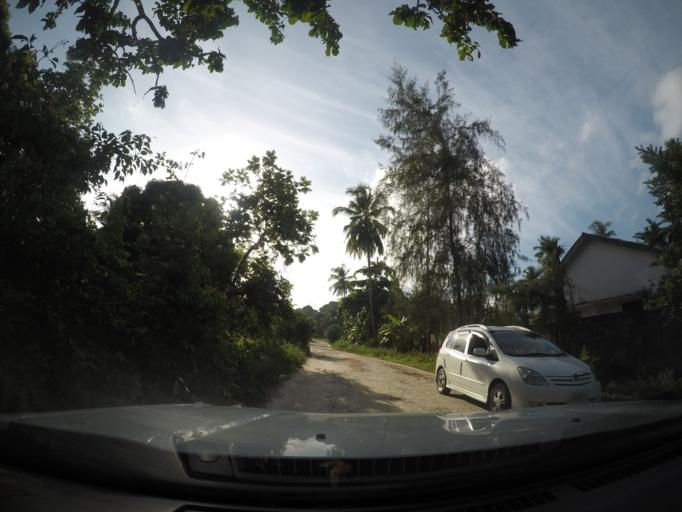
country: TZ
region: Pemba South
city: Chake Chake
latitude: -5.2487
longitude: 39.7847
